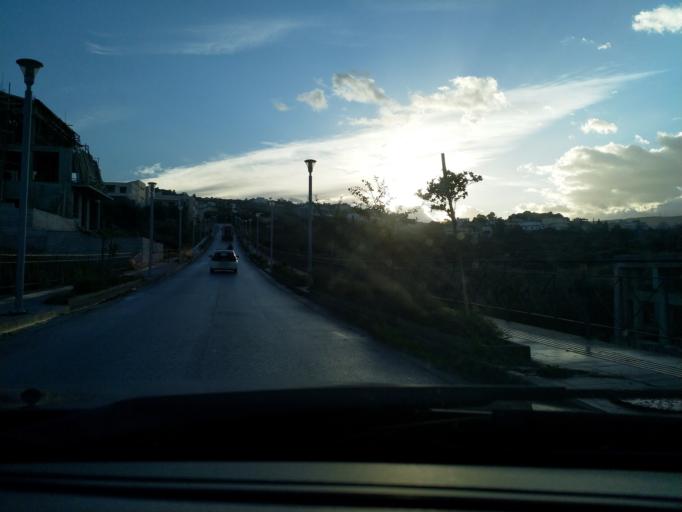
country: GR
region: Crete
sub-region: Nomos Chanias
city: Chania
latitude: 35.5124
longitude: 24.0449
